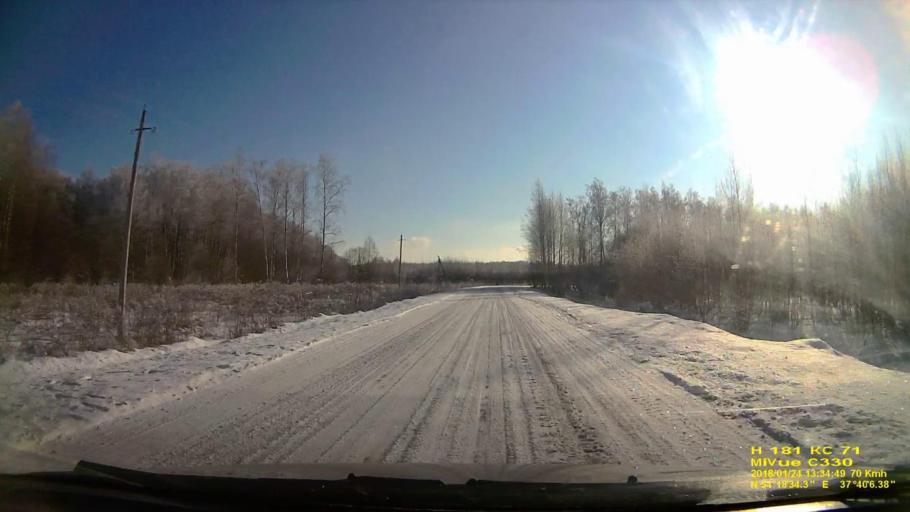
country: RU
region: Tula
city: Revyakino
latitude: 54.3094
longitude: 37.6685
